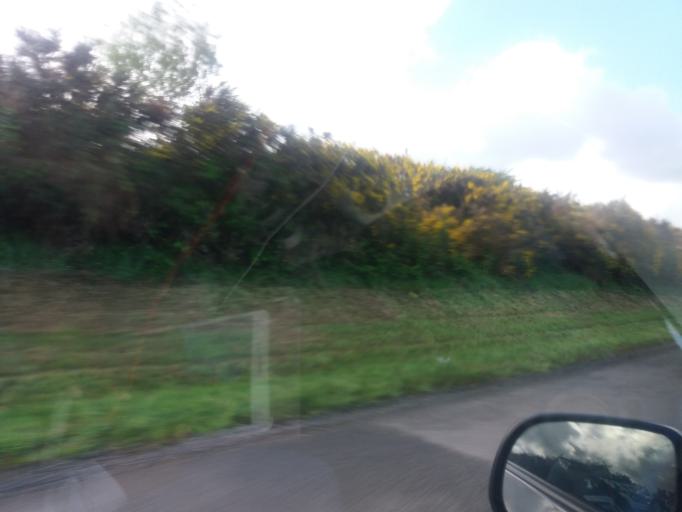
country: IE
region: Leinster
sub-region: Loch Garman
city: Gorey
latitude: 52.6482
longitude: -6.3226
